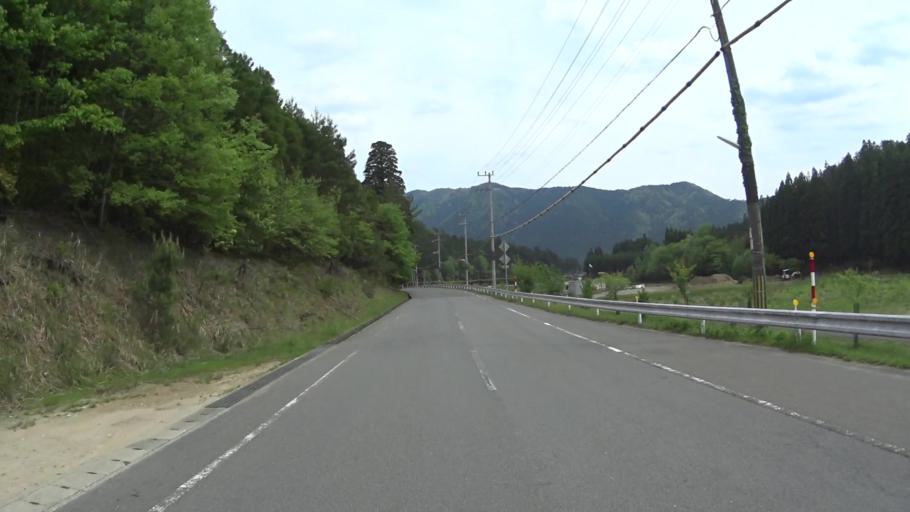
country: JP
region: Kyoto
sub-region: Kyoto-shi
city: Kamigyo-ku
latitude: 35.1859
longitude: 135.6531
